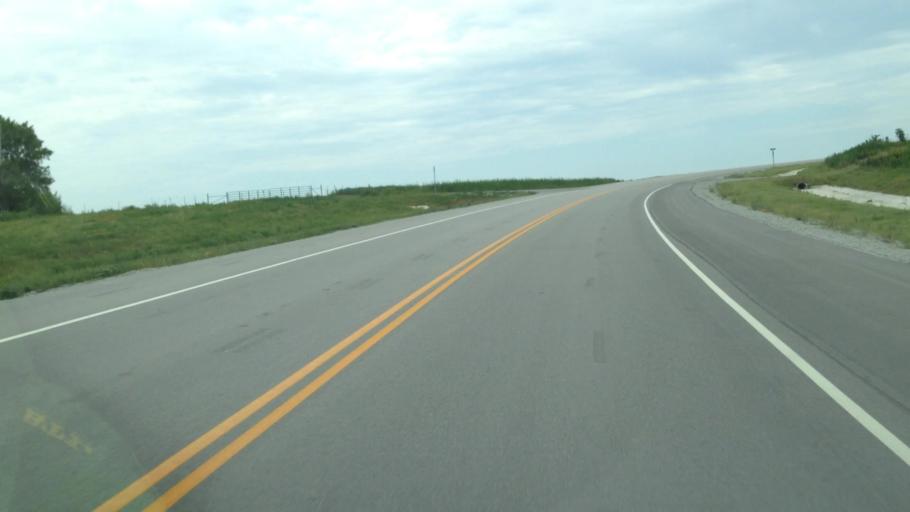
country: US
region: Kansas
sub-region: Labette County
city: Chetopa
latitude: 36.8874
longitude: -95.0984
